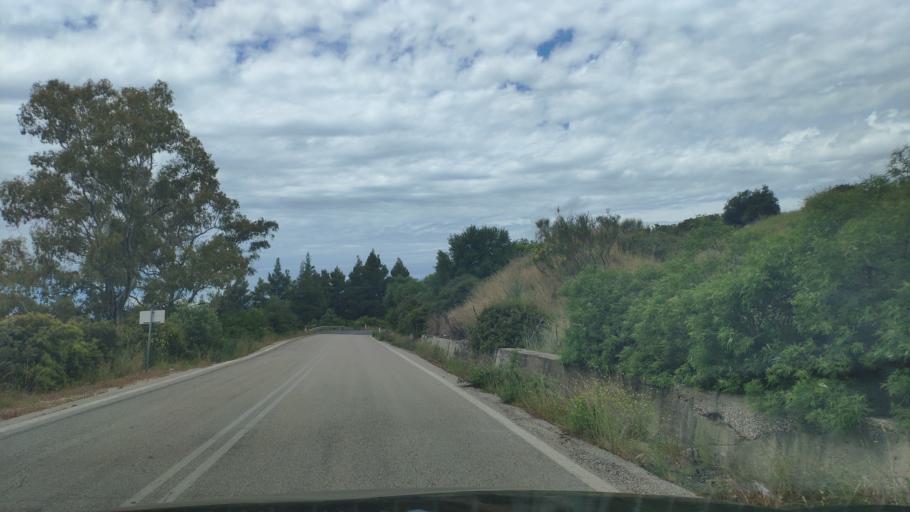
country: GR
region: West Greece
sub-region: Nomos Aitolias kai Akarnanias
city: Palairos
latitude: 38.7582
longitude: 20.8854
